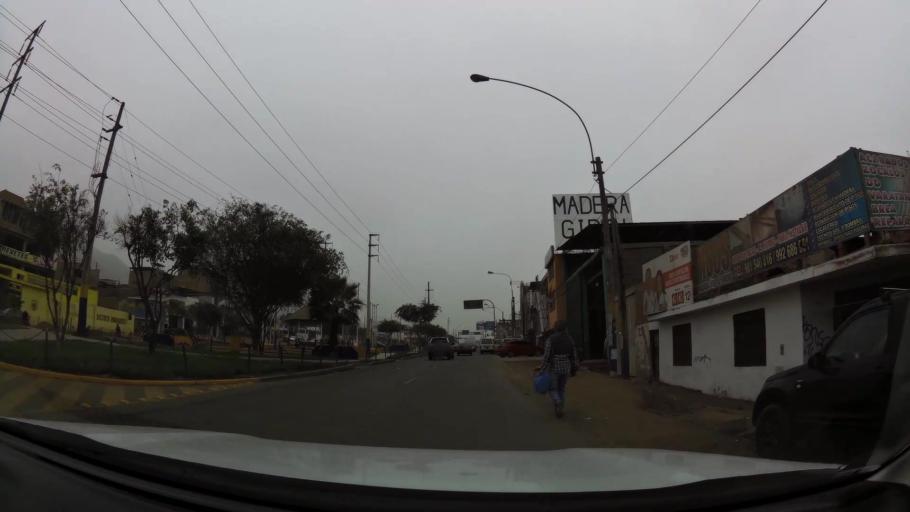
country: PE
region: Lima
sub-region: Lima
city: Surco
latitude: -12.1655
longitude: -76.9511
